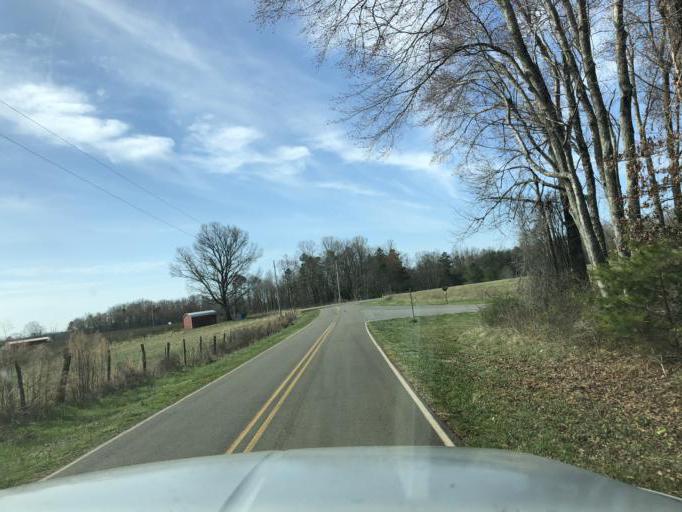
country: US
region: North Carolina
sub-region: Cleveland County
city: Shelby
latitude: 35.4808
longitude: -81.6416
